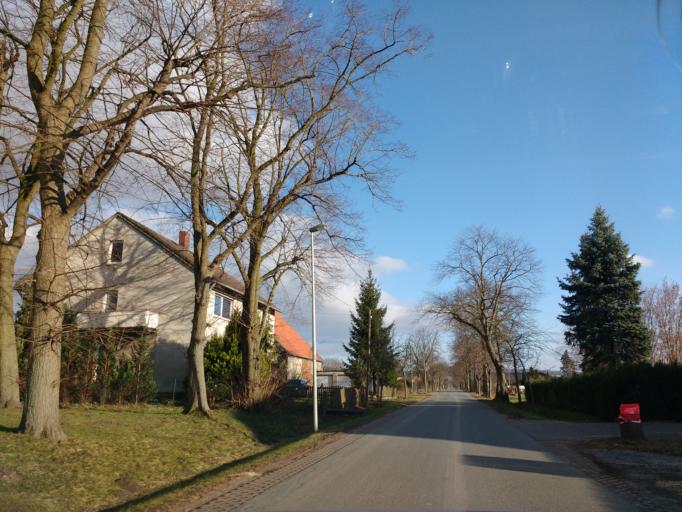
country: DE
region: North Rhine-Westphalia
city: Bad Lippspringe
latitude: 51.7768
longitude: 8.8282
